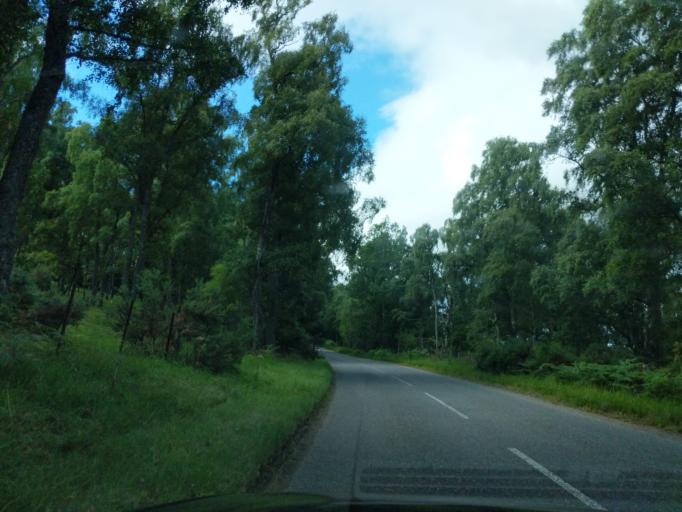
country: GB
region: Scotland
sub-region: Aberdeenshire
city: Aboyne
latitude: 57.0679
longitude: -2.9055
